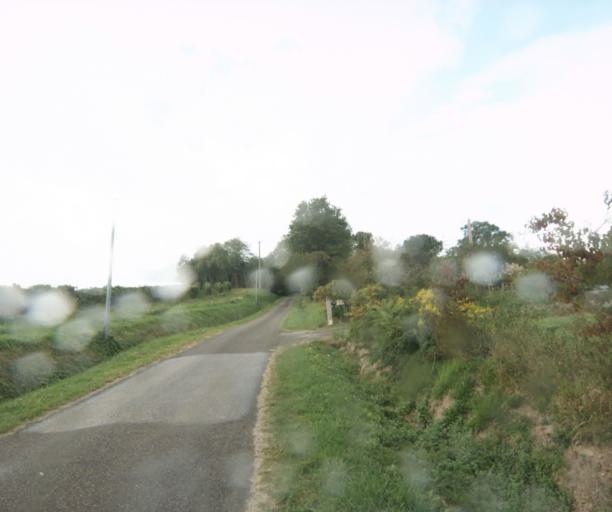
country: FR
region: Midi-Pyrenees
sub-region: Departement du Gers
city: Cazaubon
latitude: 43.8639
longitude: -0.0193
